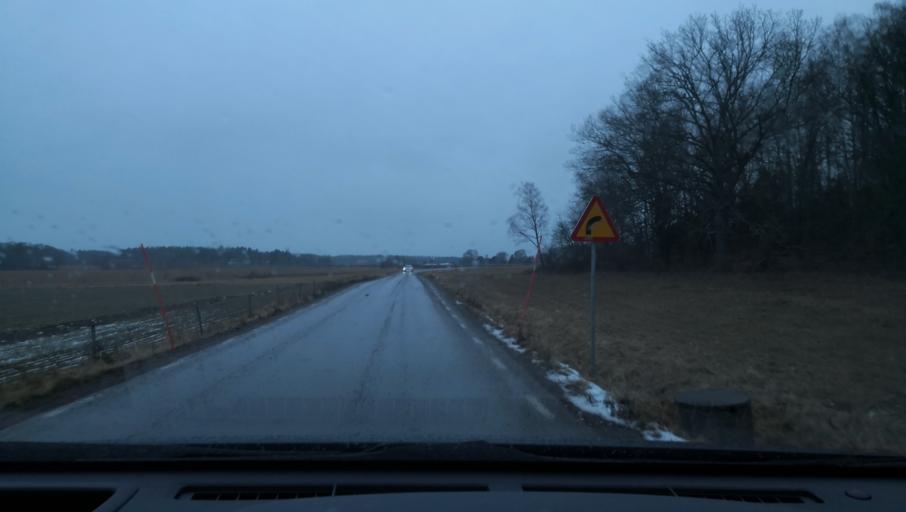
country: SE
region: Soedermanland
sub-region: Eskilstuna Kommun
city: Arla
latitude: 59.4501
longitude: 16.7401
